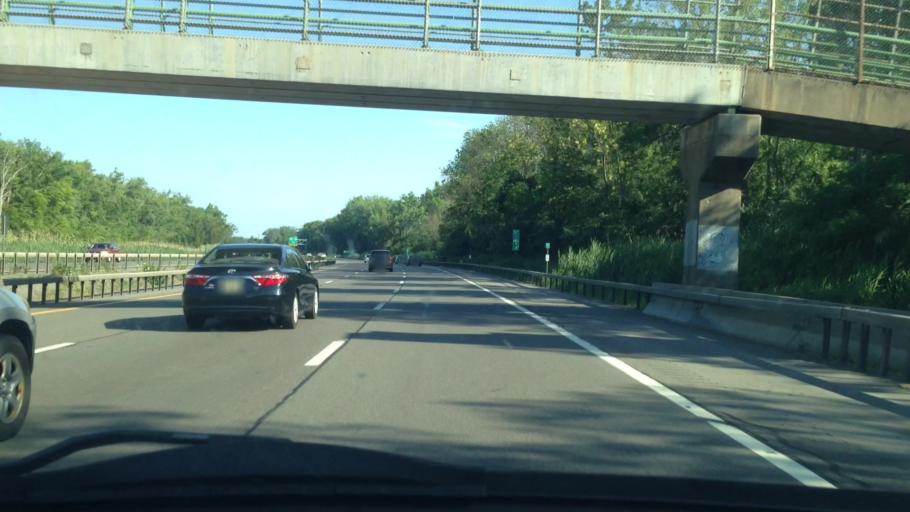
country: US
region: New York
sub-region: Onondaga County
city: Lakeland
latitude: 43.1010
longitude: -76.2430
